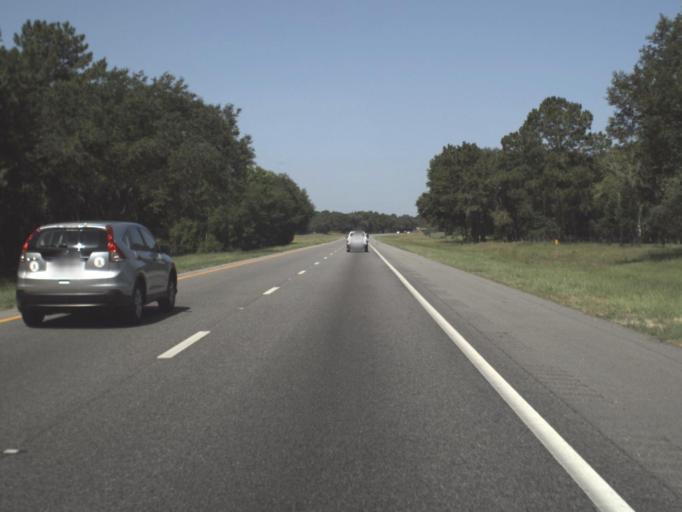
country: US
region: Florida
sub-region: Suwannee County
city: Live Oak
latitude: 30.3507
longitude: -83.0537
